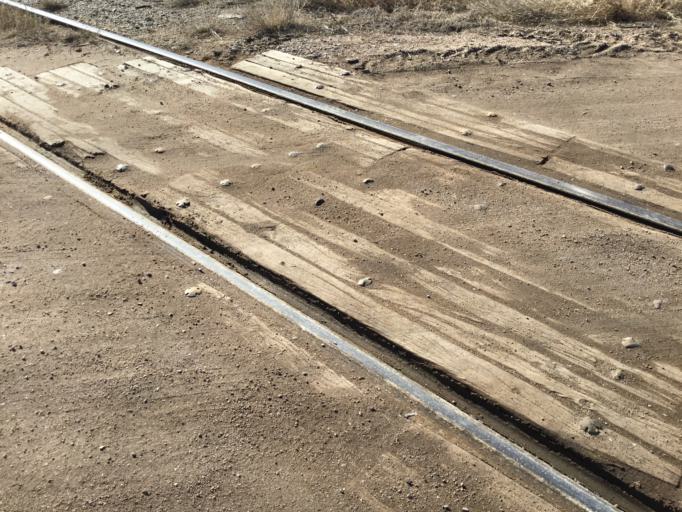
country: US
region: Kansas
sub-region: McPherson County
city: Moundridge
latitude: 38.2176
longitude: -97.5392
